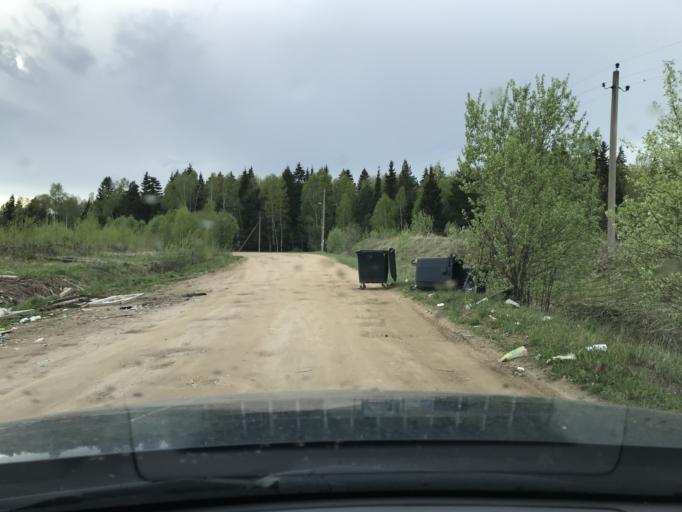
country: RU
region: Moskovskaya
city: Vereya
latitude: 55.3232
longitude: 36.3308
